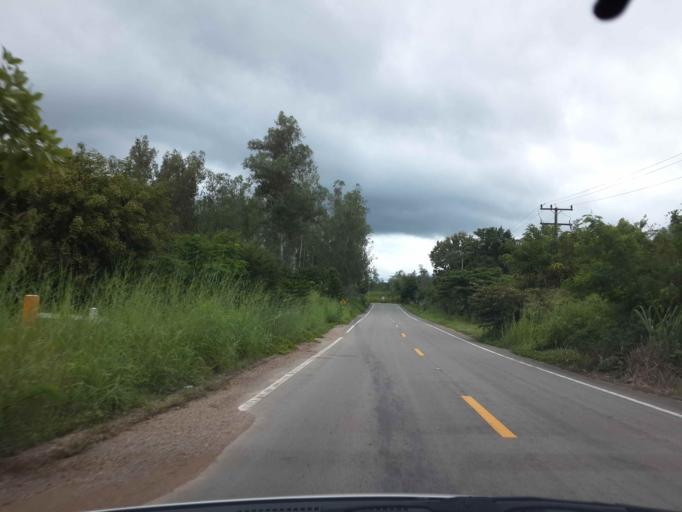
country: TH
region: Ratchaburi
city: Suan Phueng
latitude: 13.6706
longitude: 99.2029
